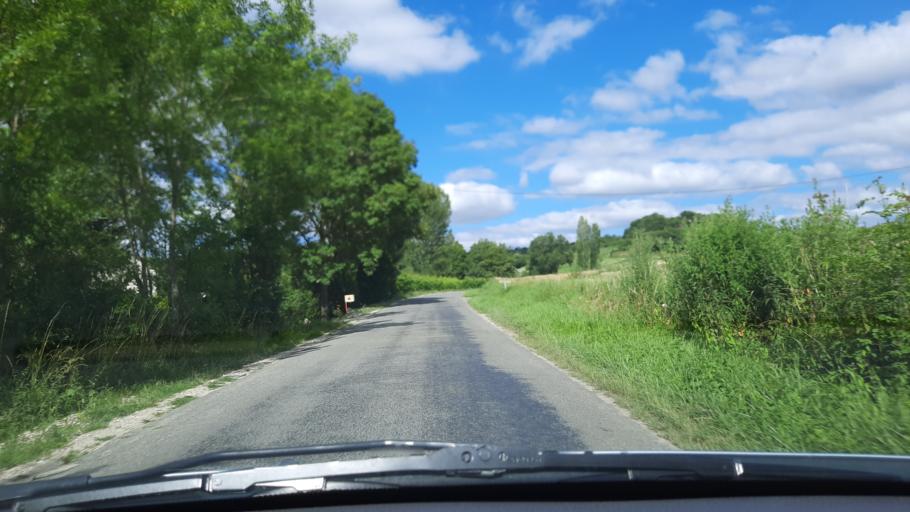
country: FR
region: Midi-Pyrenees
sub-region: Departement du Lot
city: Castelnau-Montratier
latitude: 44.2915
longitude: 1.4357
